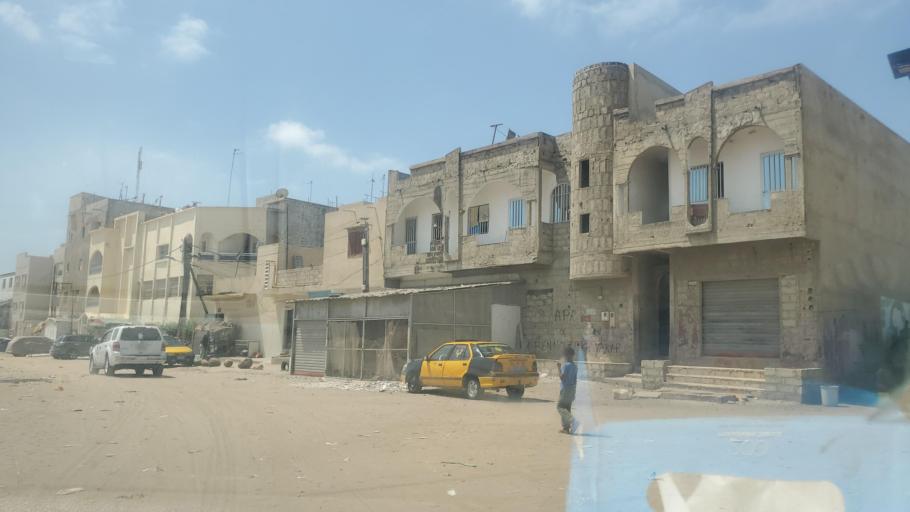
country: SN
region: Dakar
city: Grand Dakar
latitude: 14.7295
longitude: -17.4542
